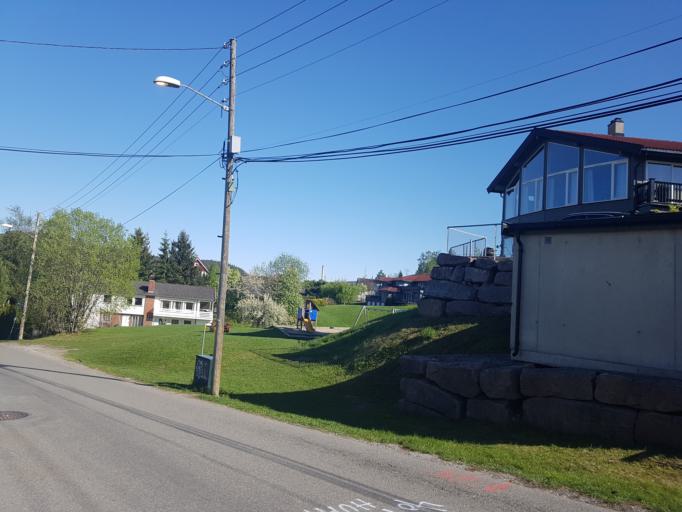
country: NO
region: Buskerud
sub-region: Drammen
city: Drammen
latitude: 59.7216
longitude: 10.2131
